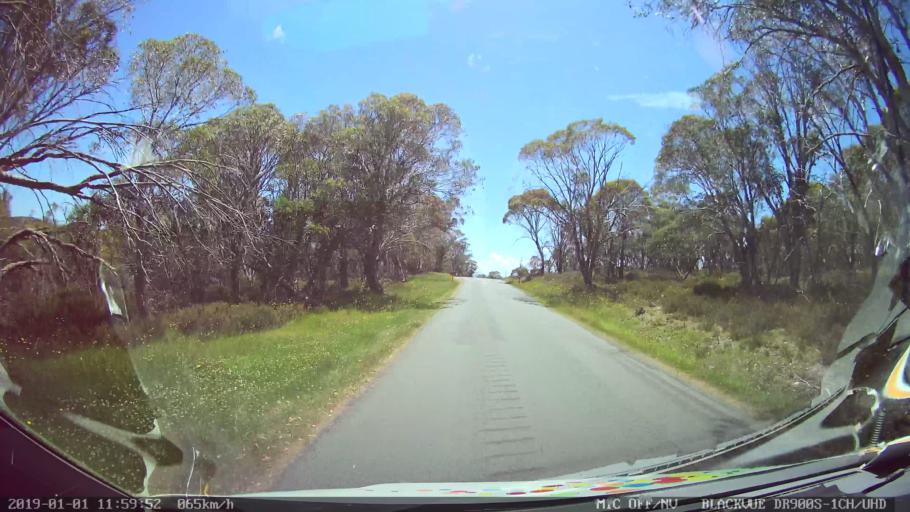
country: AU
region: New South Wales
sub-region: Snowy River
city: Jindabyne
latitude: -35.8889
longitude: 148.4551
